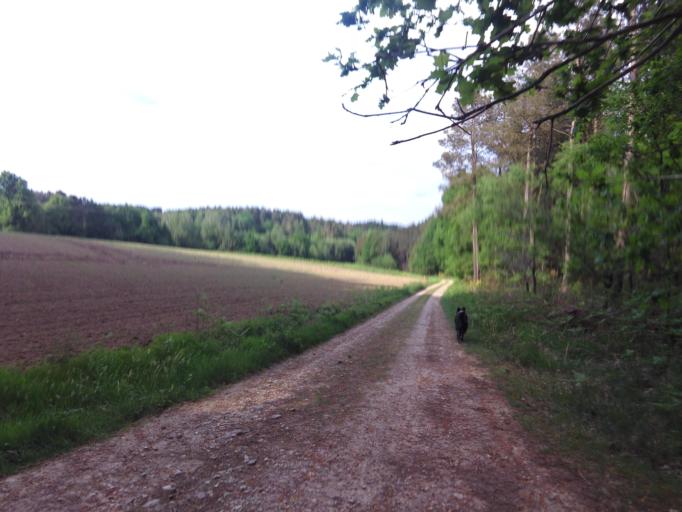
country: FR
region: Brittany
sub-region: Departement du Morbihan
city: Pleucadeuc
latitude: 47.7604
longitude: -2.4069
